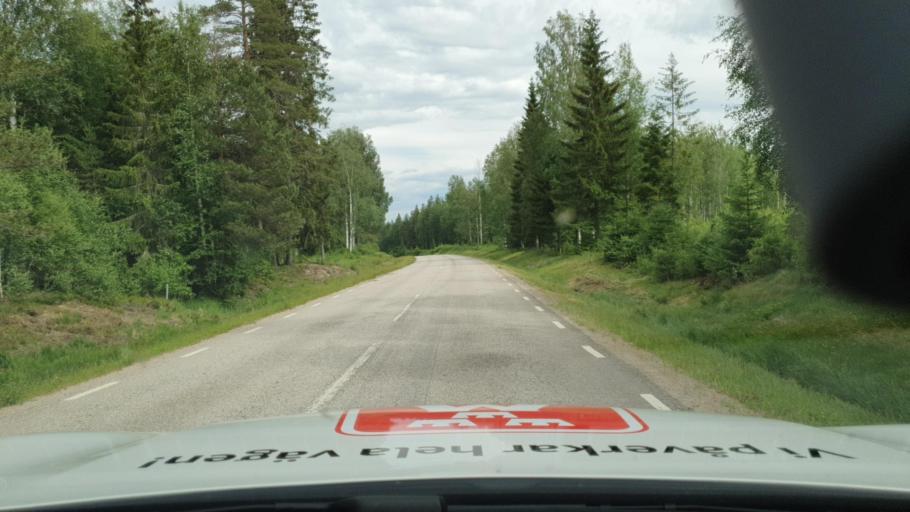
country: NO
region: Hedmark
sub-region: Trysil
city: Innbygda
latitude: 61.0191
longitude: 12.5189
